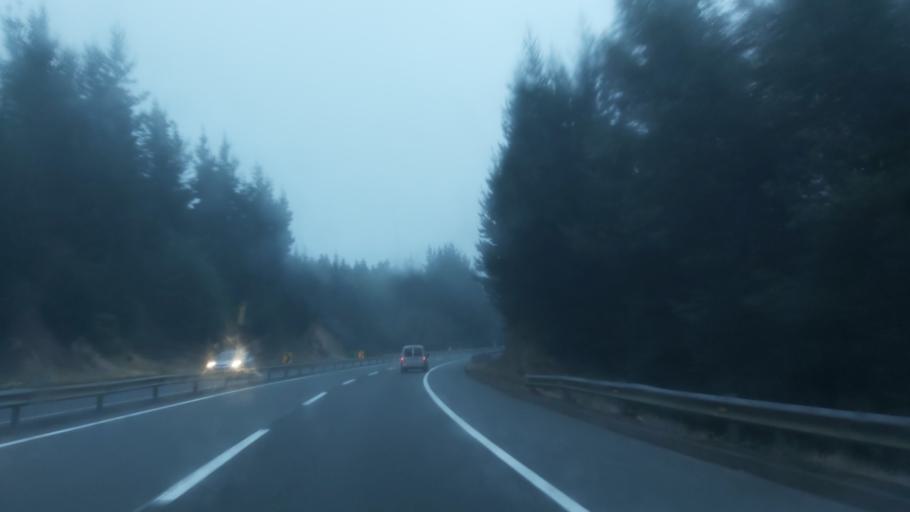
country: CL
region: Biobio
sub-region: Provincia de Concepcion
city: Penco
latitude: -36.7414
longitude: -72.9038
